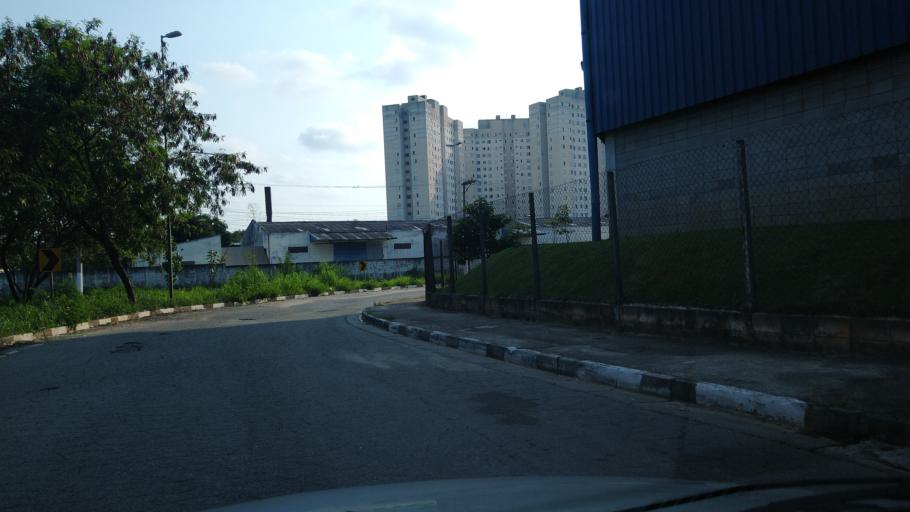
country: BR
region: Sao Paulo
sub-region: Guarulhos
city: Guarulhos
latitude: -23.4906
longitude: -46.5394
